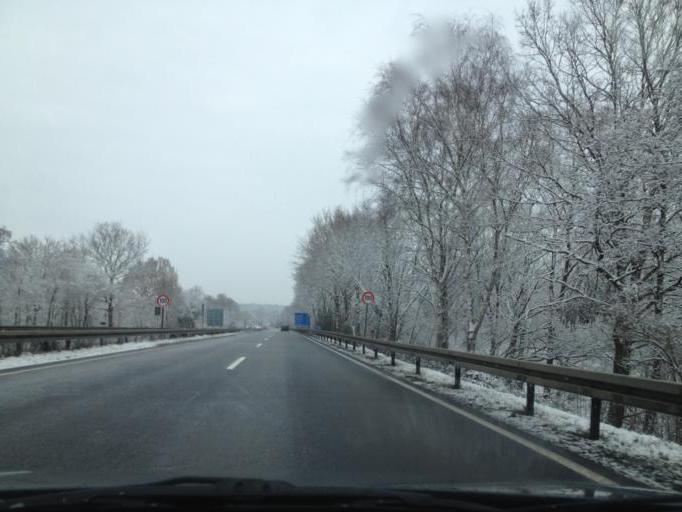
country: DE
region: Saarland
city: Homburg
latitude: 49.2752
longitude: 7.3111
